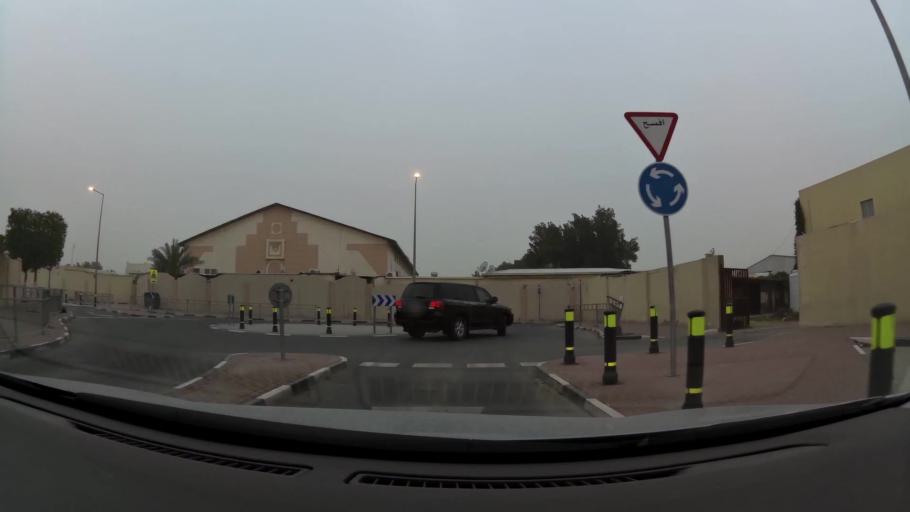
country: QA
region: Baladiyat ad Dawhah
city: Doha
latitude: 25.2297
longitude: 51.5005
